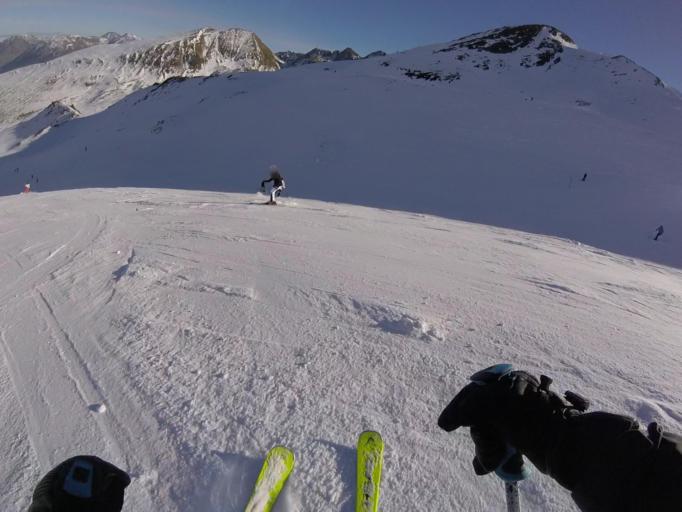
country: AD
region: Encamp
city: Pas de la Casa
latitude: 42.5293
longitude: 1.7215
